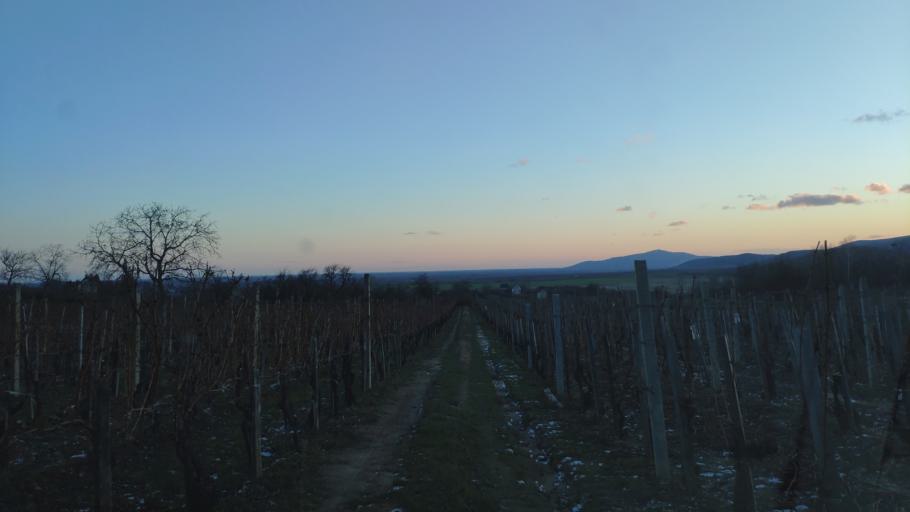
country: HU
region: Borsod-Abauj-Zemplen
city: Olaszliszka
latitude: 48.2754
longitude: 21.3969
